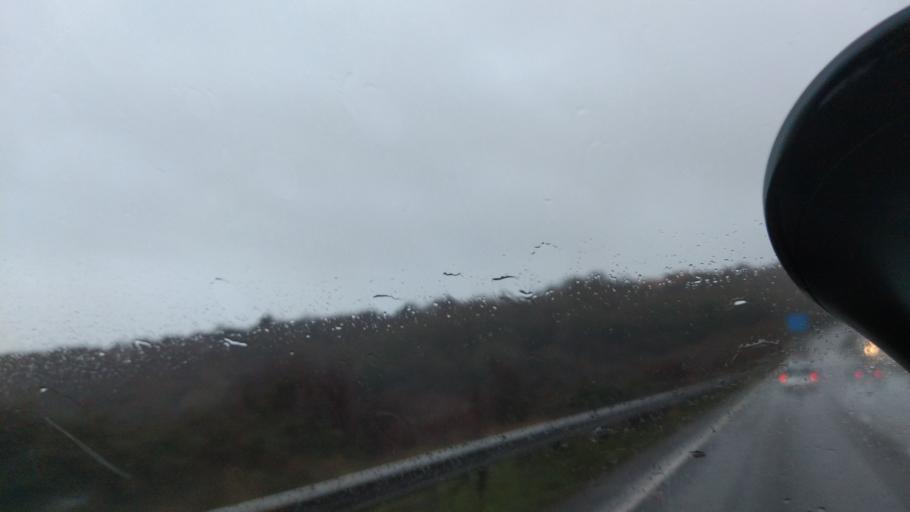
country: GB
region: England
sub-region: Brighton and Hove
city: Hove
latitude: 50.8558
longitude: -0.1850
